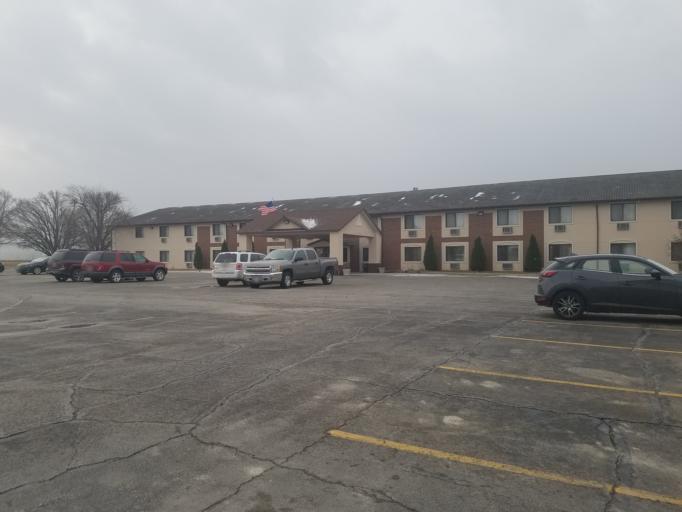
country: US
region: Iowa
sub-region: Wapello County
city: Ottumwa
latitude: 41.0639
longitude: -92.4120
